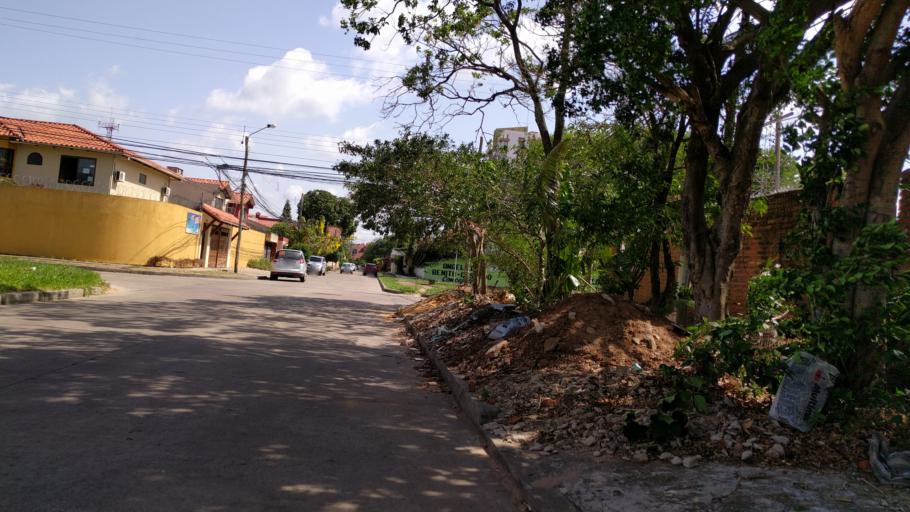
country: BO
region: Santa Cruz
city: Santa Cruz de la Sierra
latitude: -17.7880
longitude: -63.2128
